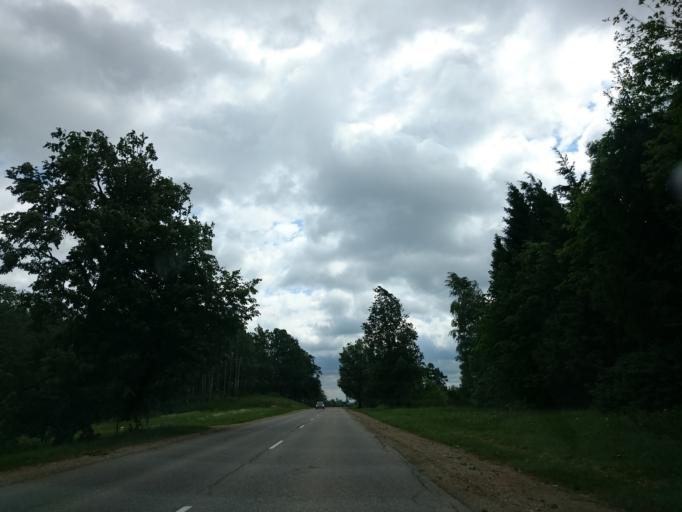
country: LV
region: Madonas Rajons
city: Madona
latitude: 56.8602
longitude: 26.1915
